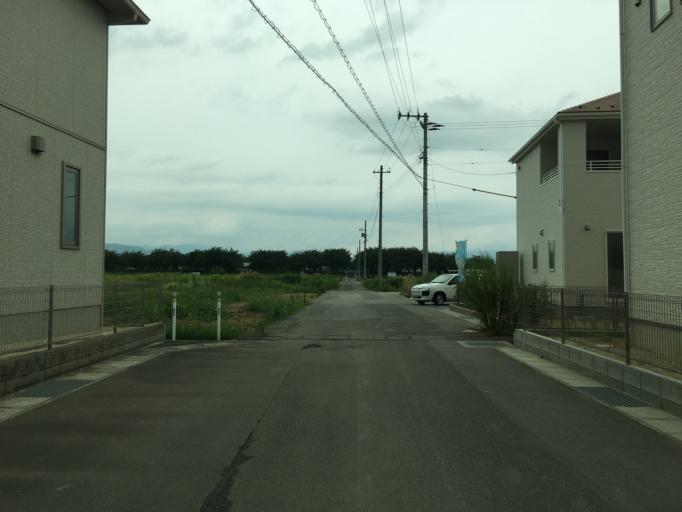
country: JP
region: Fukushima
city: Fukushima-shi
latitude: 37.7518
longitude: 140.4409
